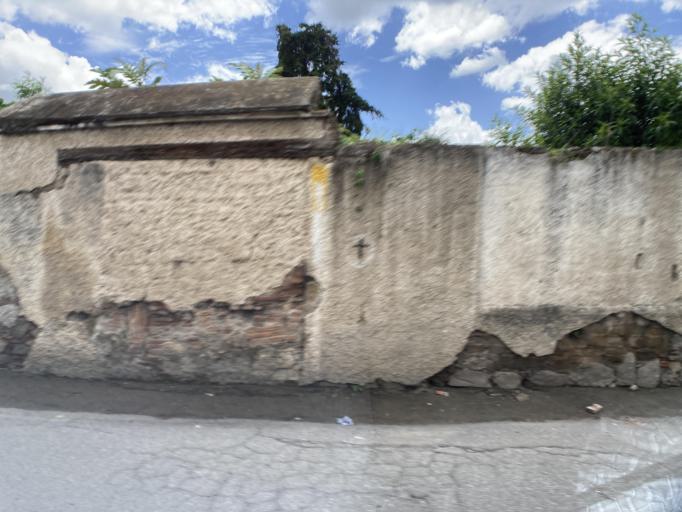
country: GT
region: Sacatepequez
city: Antigua Guatemala
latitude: 14.5544
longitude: -90.7420
